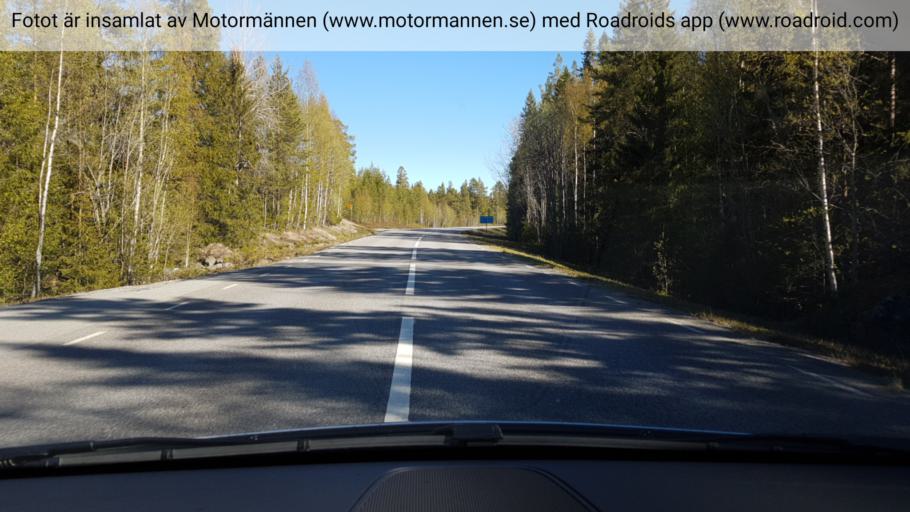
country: SE
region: Jaemtland
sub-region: Stroemsunds Kommun
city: Stroemsund
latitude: 64.3343
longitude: 15.1627
